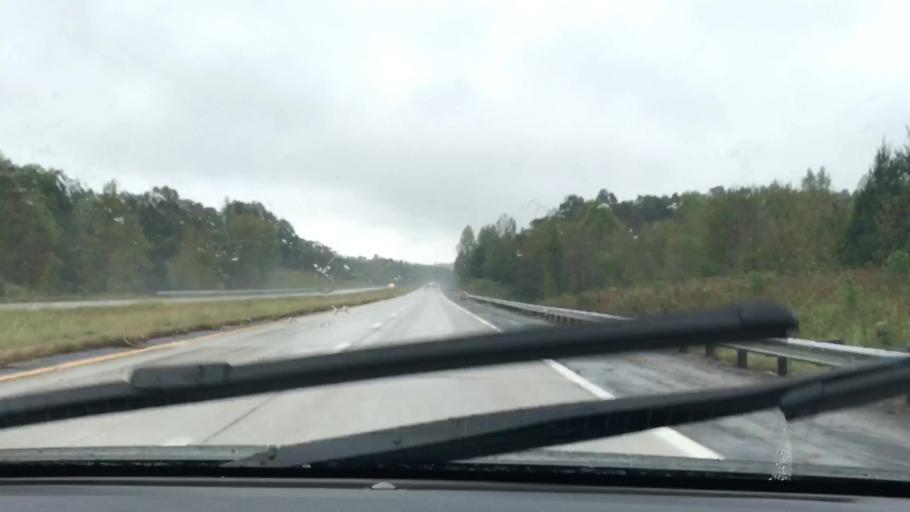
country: US
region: Kentucky
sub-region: Hopkins County
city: Nortonville
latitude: 37.1384
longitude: -87.4609
